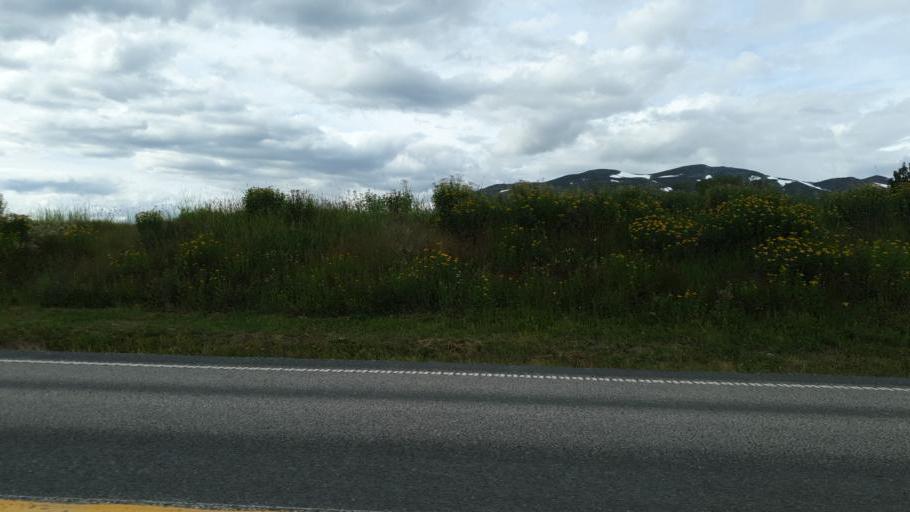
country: NO
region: Sor-Trondelag
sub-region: Oppdal
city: Oppdal
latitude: 62.5794
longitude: 9.6619
